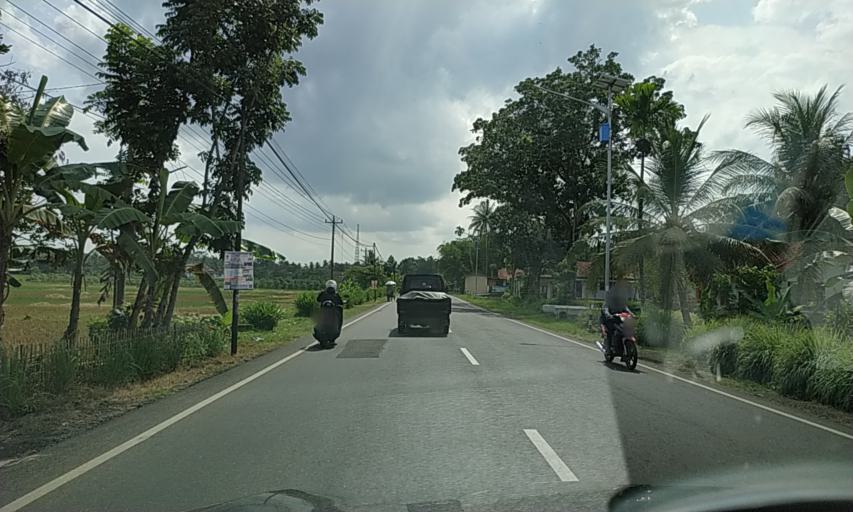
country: ID
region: Central Java
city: Cihandiwung Lor
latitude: -7.3367
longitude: 108.6960
